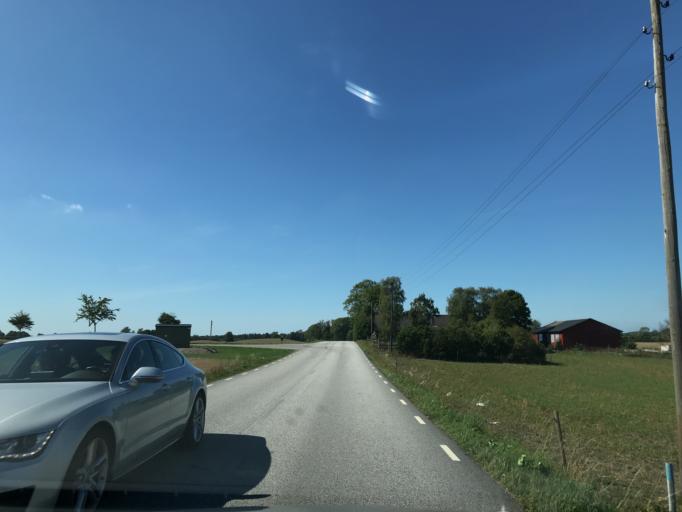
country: SE
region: Skane
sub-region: Tomelilla Kommun
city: Tomelilla
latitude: 55.6459
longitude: 13.9754
